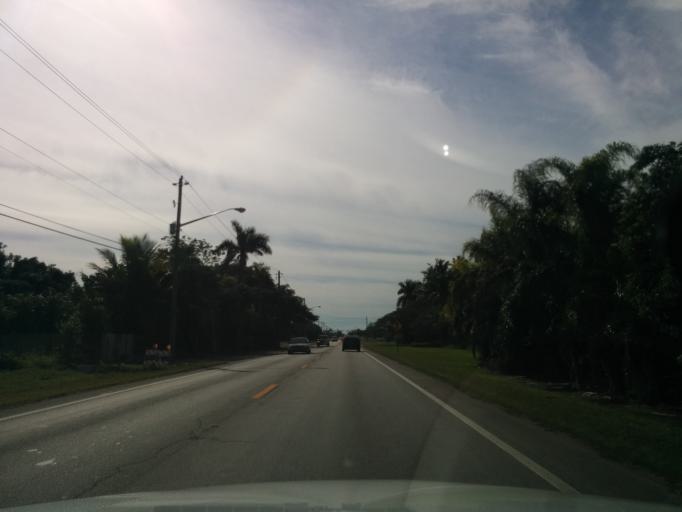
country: US
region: Florida
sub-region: Miami-Dade County
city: Homestead
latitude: 25.5031
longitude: -80.4777
